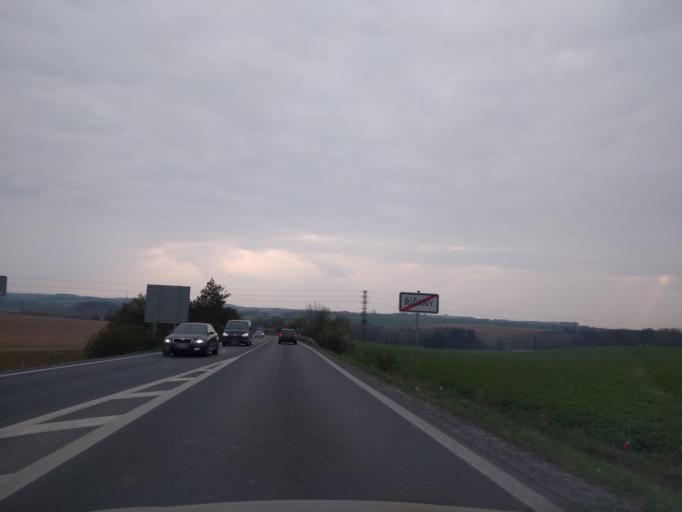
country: CZ
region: Central Bohemia
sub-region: Okres Praha-Vychod
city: Ricany
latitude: 49.9859
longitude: 14.6397
